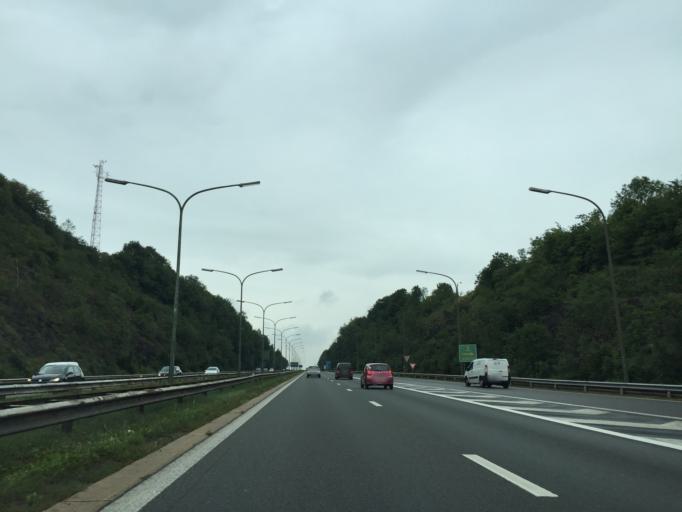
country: BE
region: Wallonia
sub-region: Province de Liege
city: Dison
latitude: 50.5973
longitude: 5.8456
